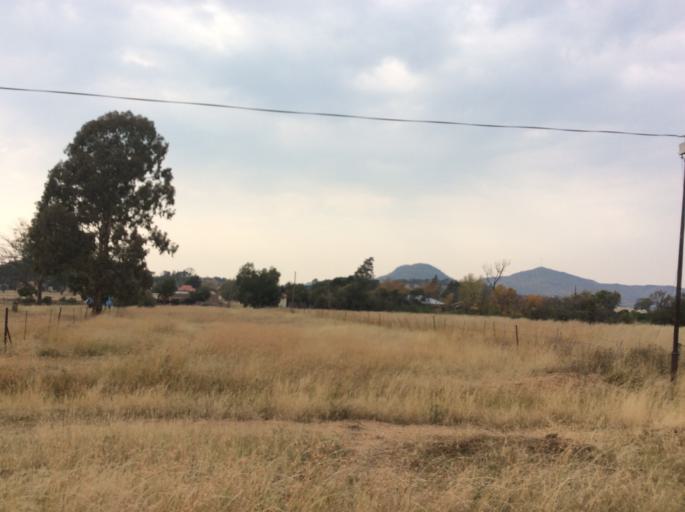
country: LS
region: Mafeteng
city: Mafeteng
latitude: -29.9890
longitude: 27.0132
